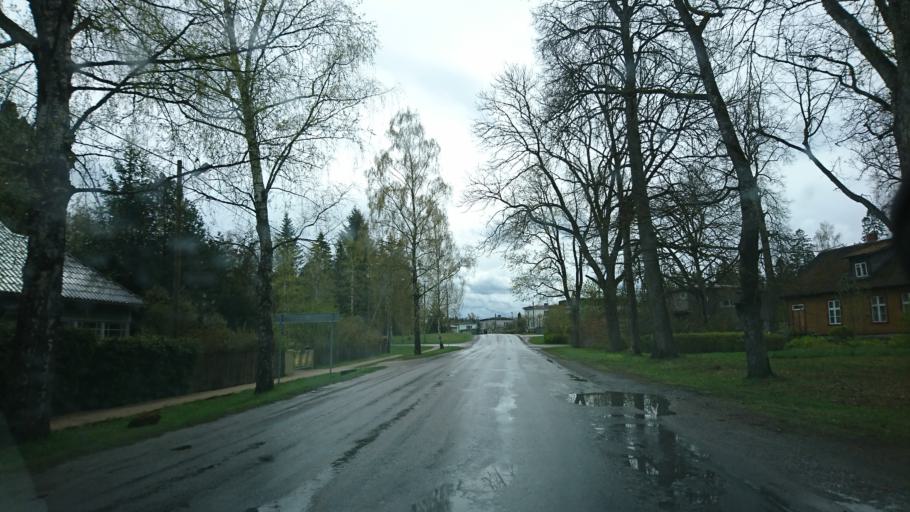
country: EE
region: Laeaene-Virumaa
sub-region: Rakvere linn
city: Rakvere
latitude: 59.3276
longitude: 26.3639
